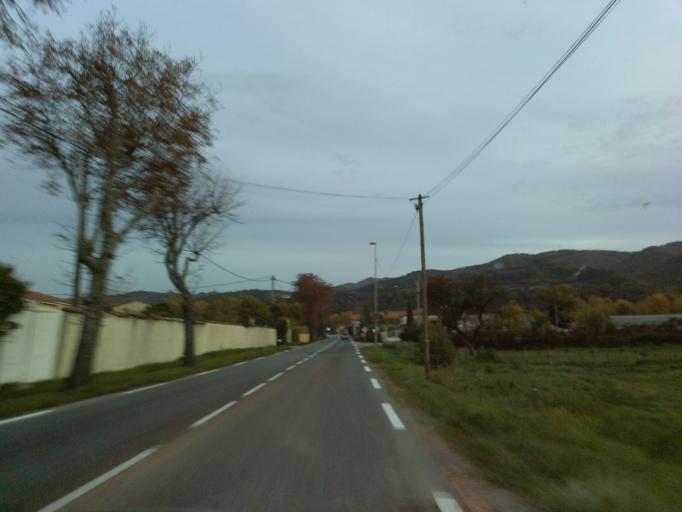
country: FR
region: Provence-Alpes-Cote d'Azur
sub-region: Departement des Alpes-de-Haute-Provence
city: Malijai
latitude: 44.0502
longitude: 6.0249
